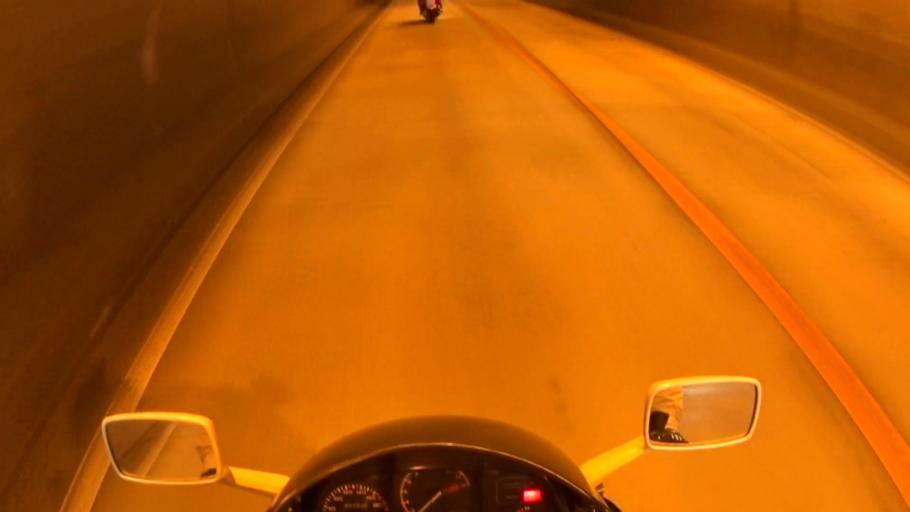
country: JP
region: Kyoto
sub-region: Kyoto-shi
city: Kamigyo-ku
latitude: 35.0786
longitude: 135.6867
